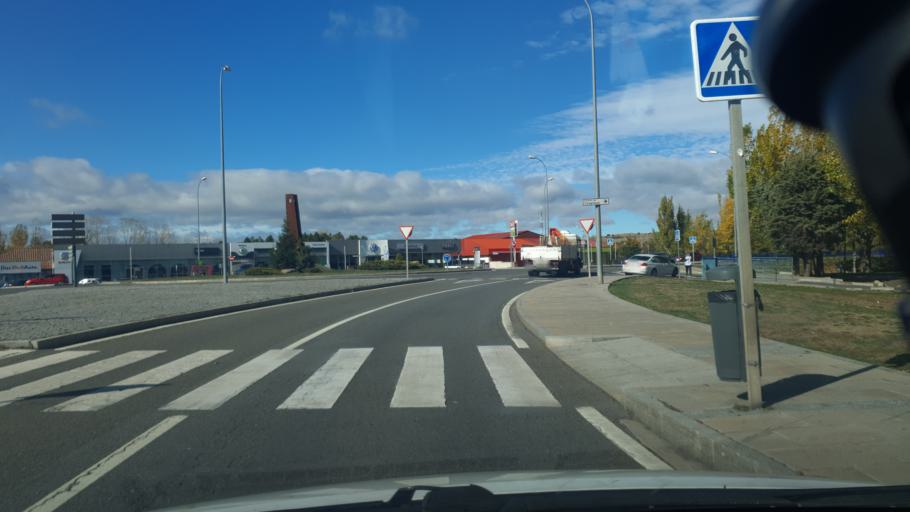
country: ES
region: Castille and Leon
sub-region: Provincia de Avila
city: Avila
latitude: 40.6457
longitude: -4.7038
